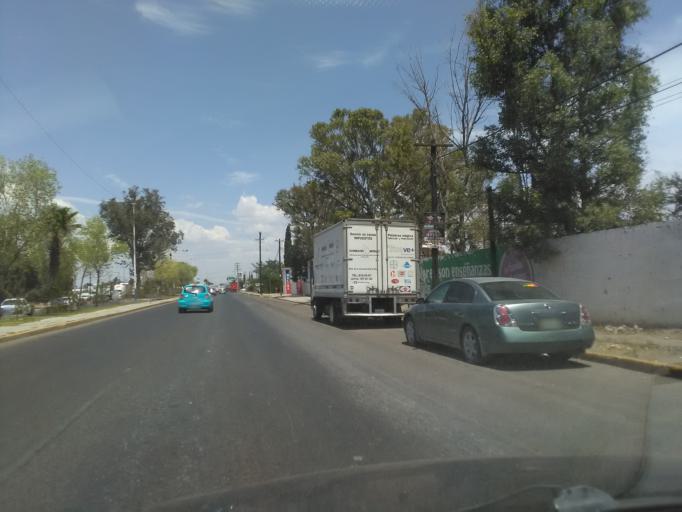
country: MX
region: Durango
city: Victoria de Durango
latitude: 24.0306
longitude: -104.6162
